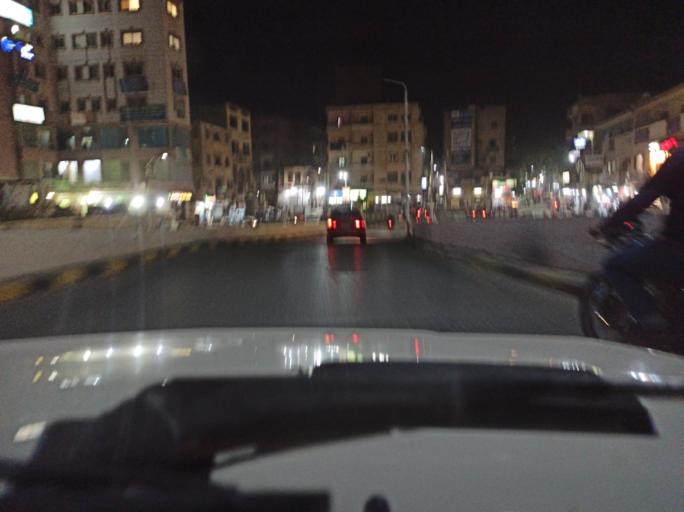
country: EG
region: Muhafazat Bani Suwayf
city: Bani Suwayf
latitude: 29.0752
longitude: 31.0939
